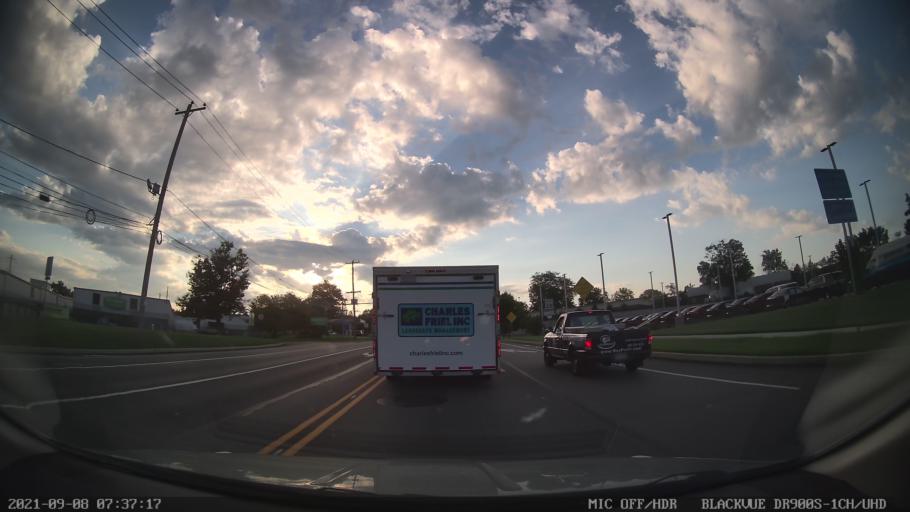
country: US
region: Pennsylvania
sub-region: Montgomery County
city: King of Prussia
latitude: 40.0831
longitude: -75.3827
